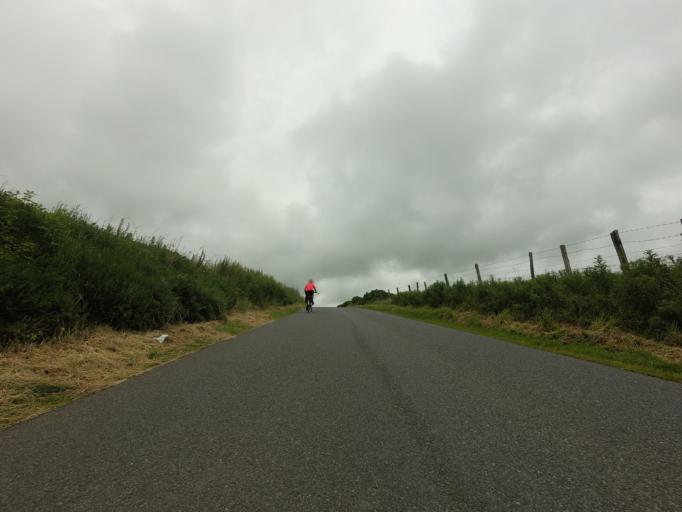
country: GB
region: Scotland
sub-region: Aberdeenshire
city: Turriff
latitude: 57.5423
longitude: -2.2681
